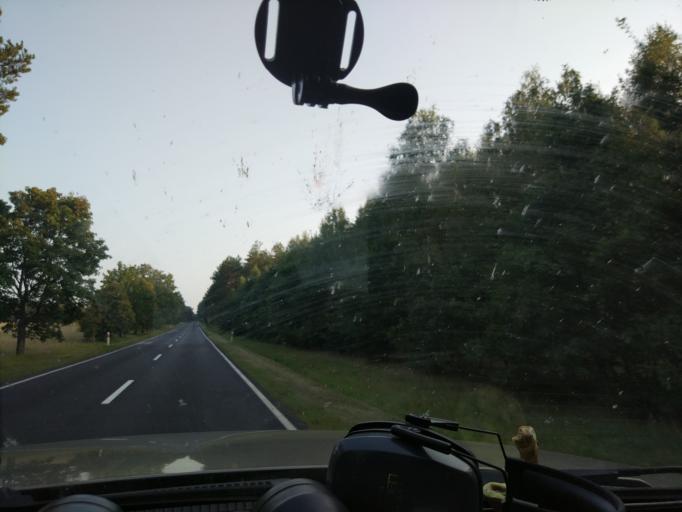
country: PL
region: Warmian-Masurian Voivodeship
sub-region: Powiat szczycienski
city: Wielbark
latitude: 53.3402
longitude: 20.9014
